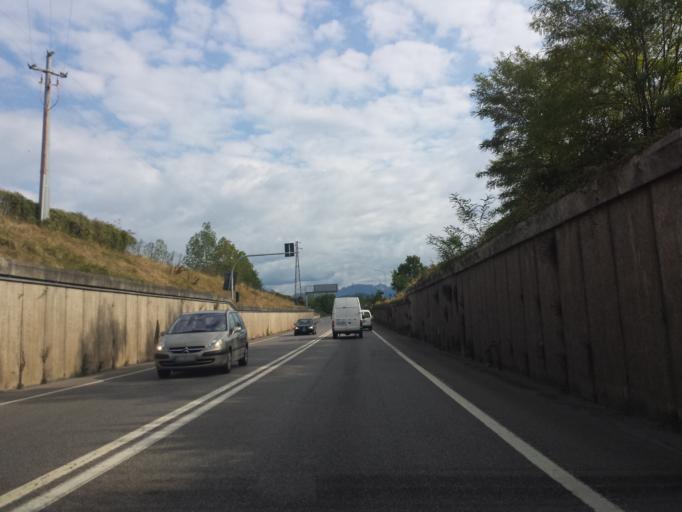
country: IT
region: Lombardy
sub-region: Provincia di Brescia
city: Prevalle
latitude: 45.5483
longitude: 10.4296
